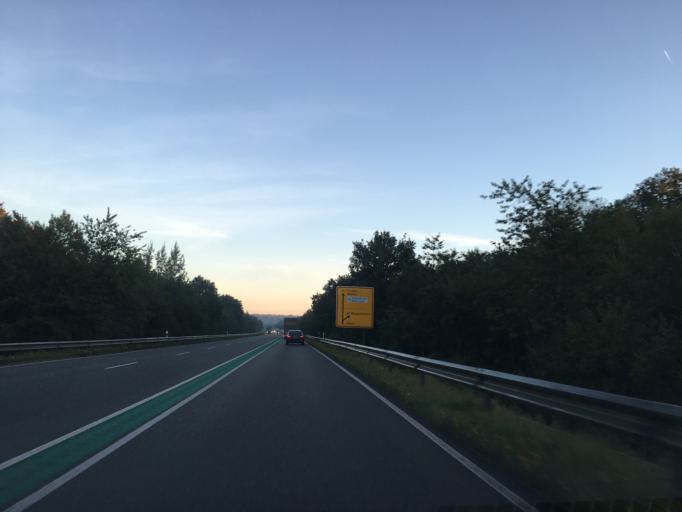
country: DE
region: North Rhine-Westphalia
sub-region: Regierungsbezirk Munster
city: Steinfurt
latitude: 52.1316
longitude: 7.3672
